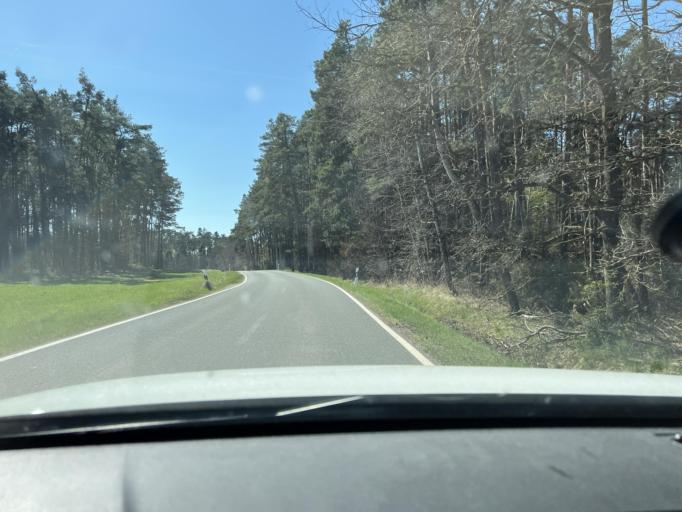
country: DE
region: Bavaria
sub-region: Regierungsbezirk Mittelfranken
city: Grosshabersdorf
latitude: 49.4341
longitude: 10.7734
